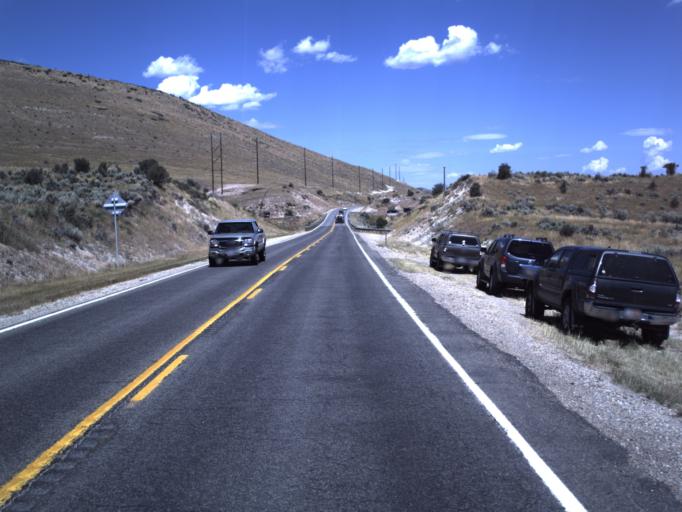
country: US
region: Utah
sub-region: Summit County
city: Oakley
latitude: 40.7736
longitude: -111.4078
